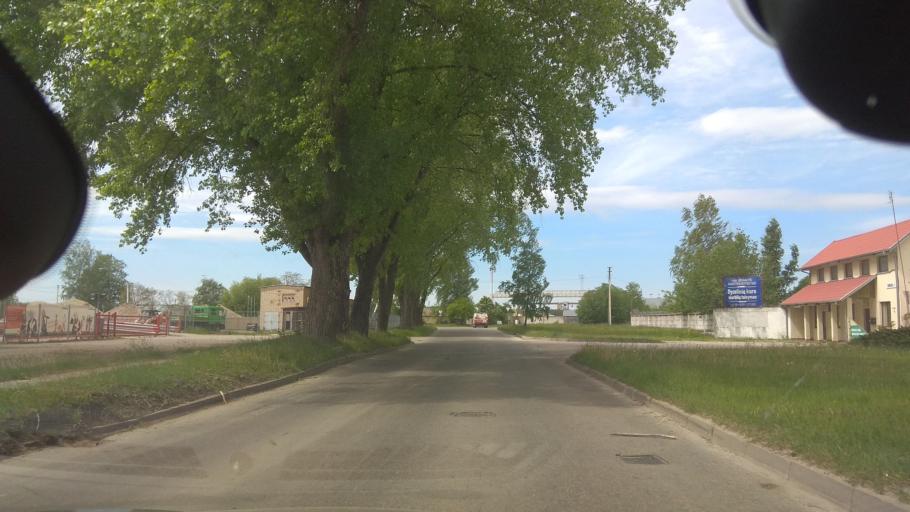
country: LT
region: Kauno apskritis
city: Jonava
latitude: 55.0912
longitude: 24.2822
